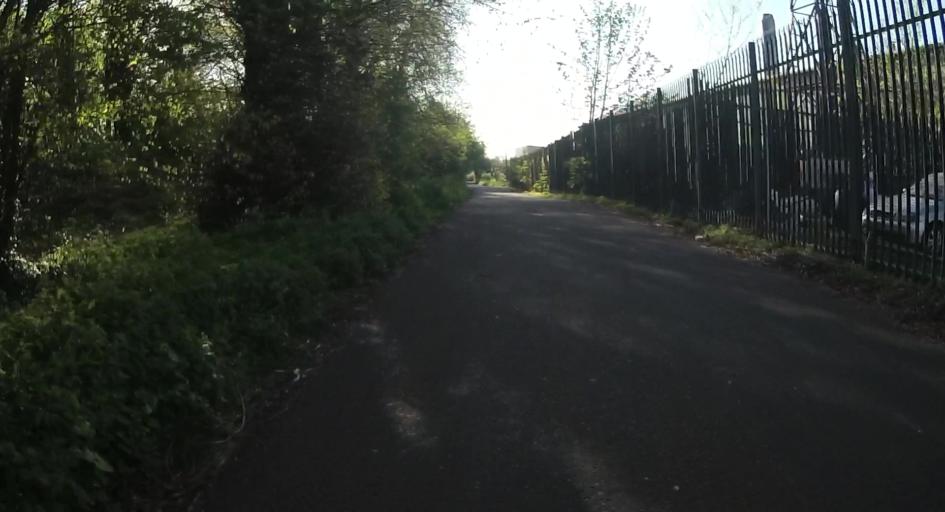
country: GB
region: England
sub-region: Hampshire
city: Basingstoke
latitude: 51.2638
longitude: -1.1129
